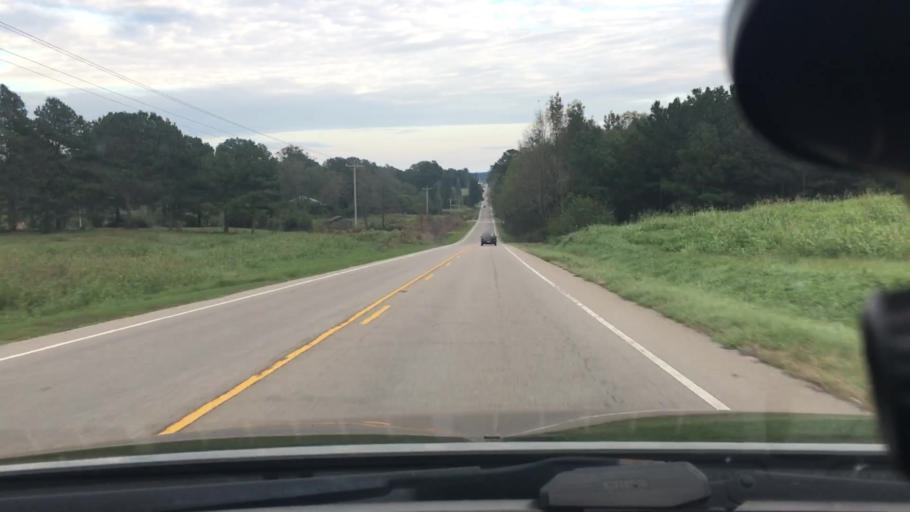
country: US
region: North Carolina
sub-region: Moore County
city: Robbins
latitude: 35.3913
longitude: -79.5164
